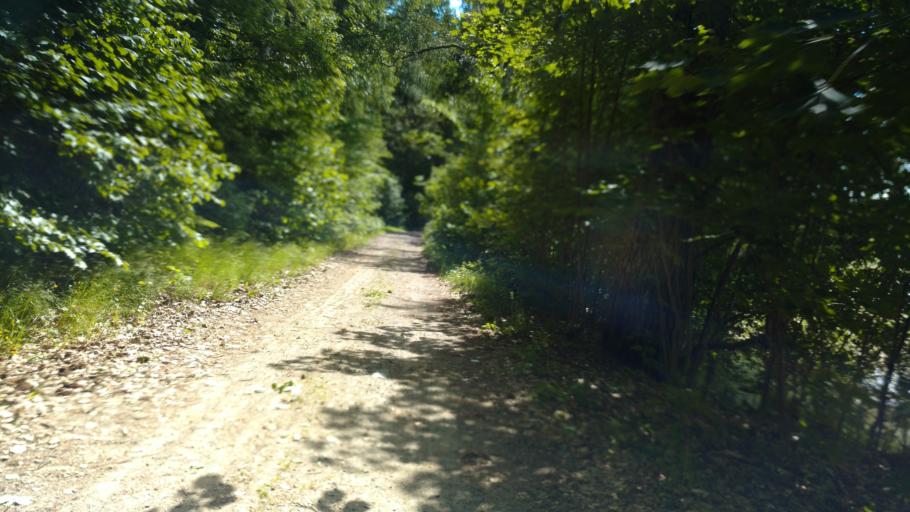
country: FI
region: Uusimaa
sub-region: Raaseporin
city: Pohja
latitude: 60.1116
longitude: 23.5459
